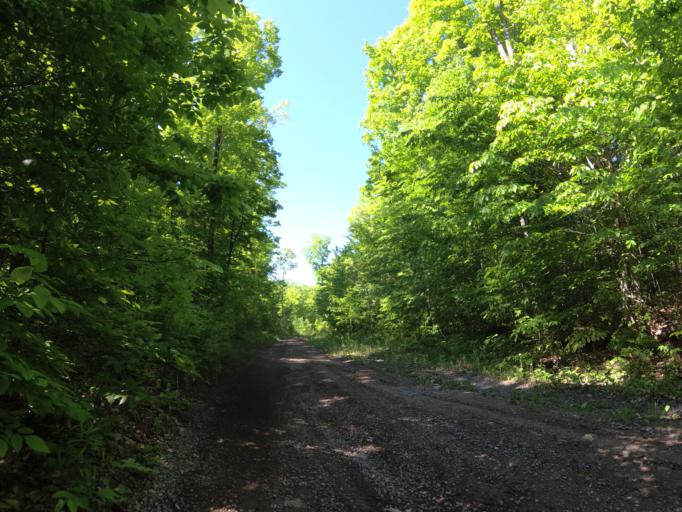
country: CA
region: Ontario
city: Renfrew
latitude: 45.0956
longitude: -77.0715
